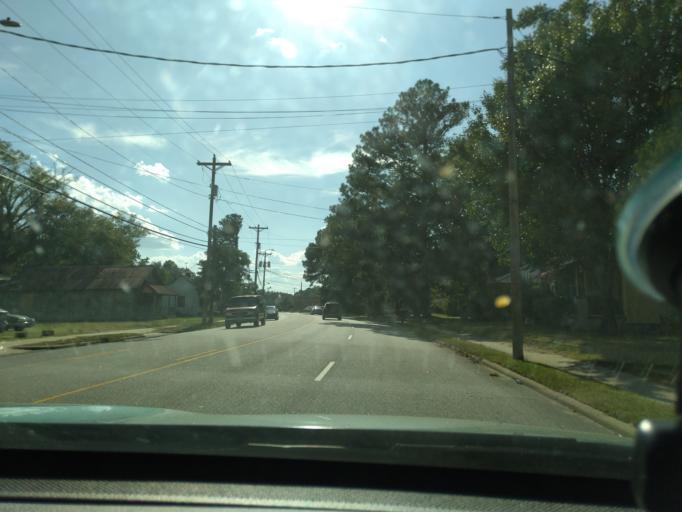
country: US
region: North Carolina
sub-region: Nash County
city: Rocky Mount
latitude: 35.9350
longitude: -77.8079
